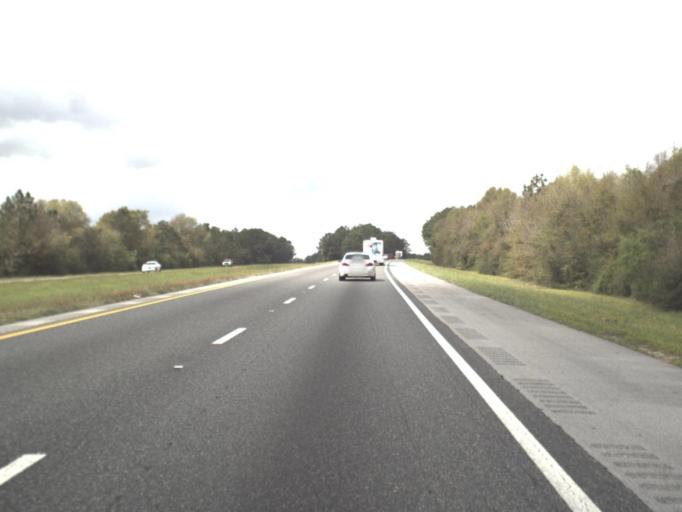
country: US
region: Florida
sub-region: Okaloosa County
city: Crestview
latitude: 30.7162
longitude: -86.6123
